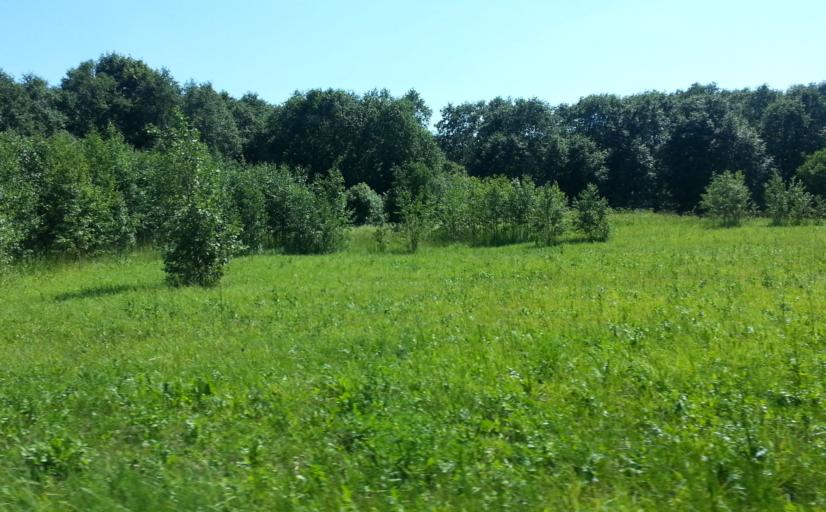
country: LT
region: Panevezys
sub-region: Birzai
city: Birzai
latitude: 56.2101
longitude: 24.6915
